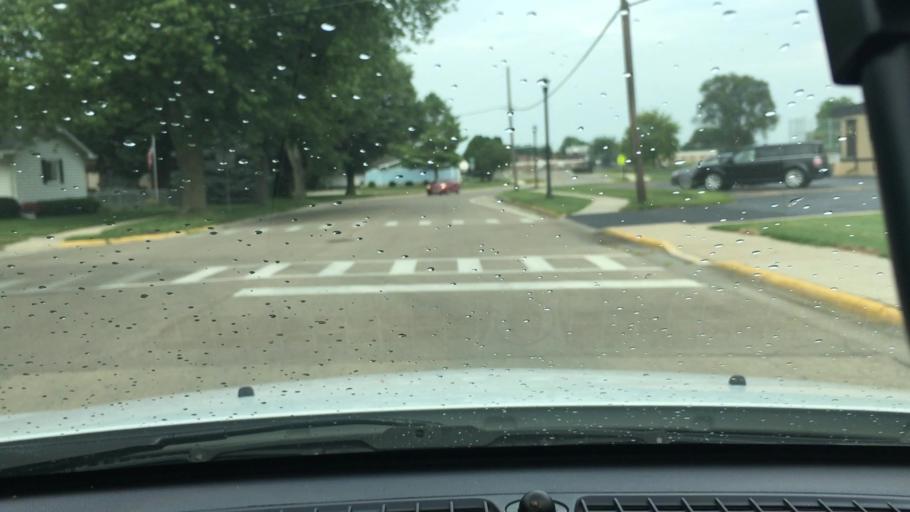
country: US
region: Illinois
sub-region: Ogle County
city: Rochelle
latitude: 41.9304
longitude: -89.0620
